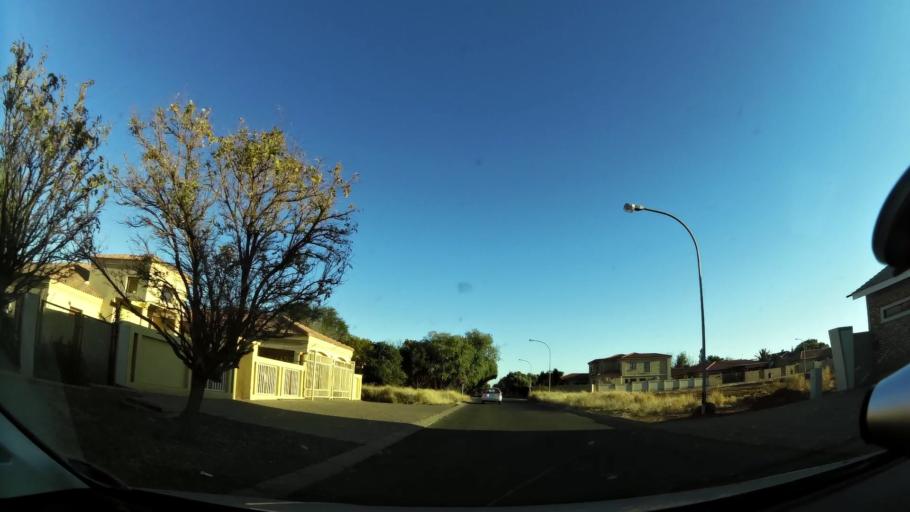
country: ZA
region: Northern Cape
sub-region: Frances Baard District Municipality
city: Kimberley
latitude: -28.7601
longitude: 24.7356
